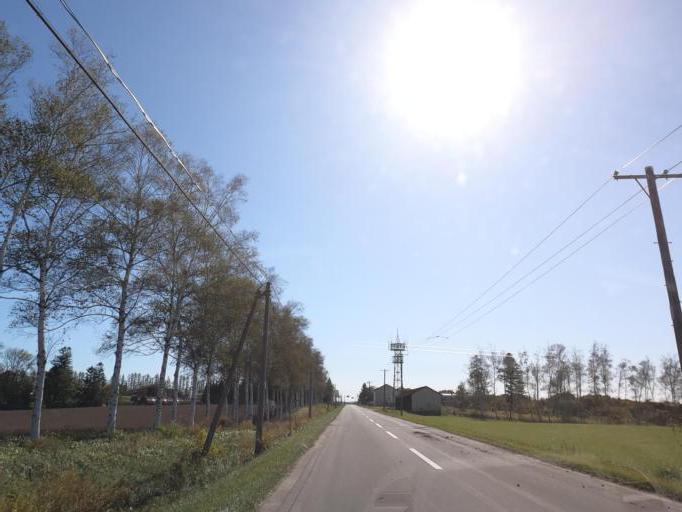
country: JP
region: Hokkaido
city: Obihiro
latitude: 42.8341
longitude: 143.2563
